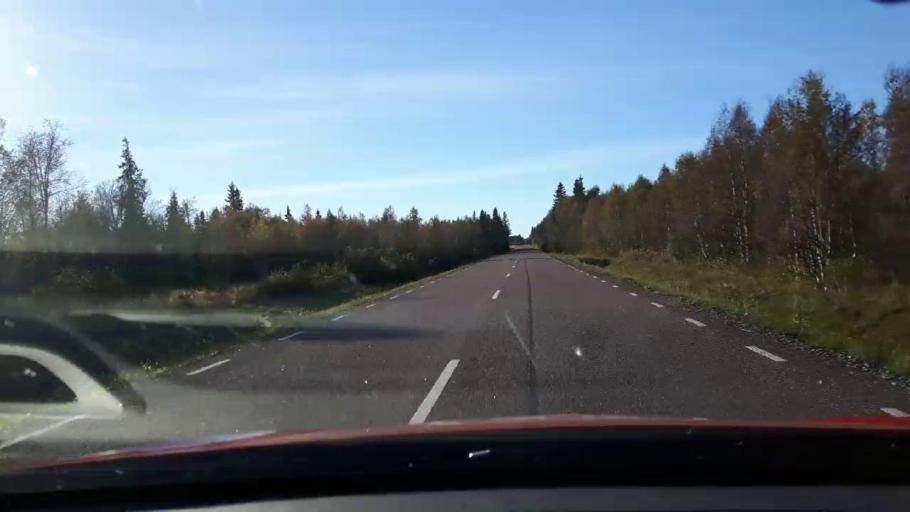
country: SE
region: Jaemtland
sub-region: Stroemsunds Kommun
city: Stroemsund
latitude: 63.8616
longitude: 15.1721
